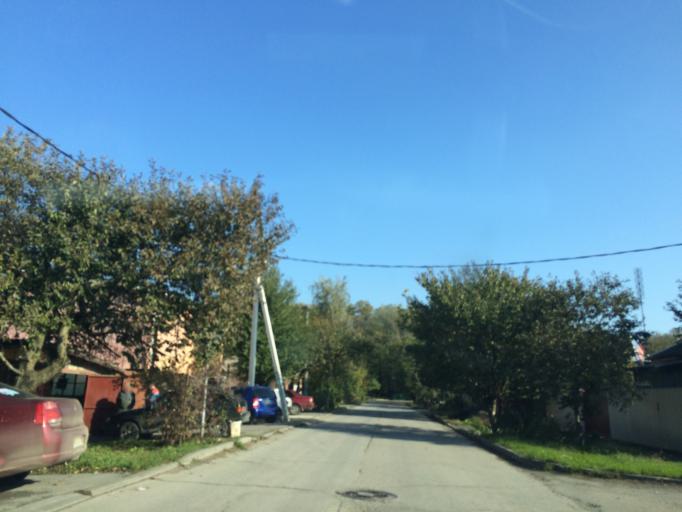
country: RU
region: Rostov
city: Imeni Chkalova
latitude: 47.2730
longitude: 39.7953
